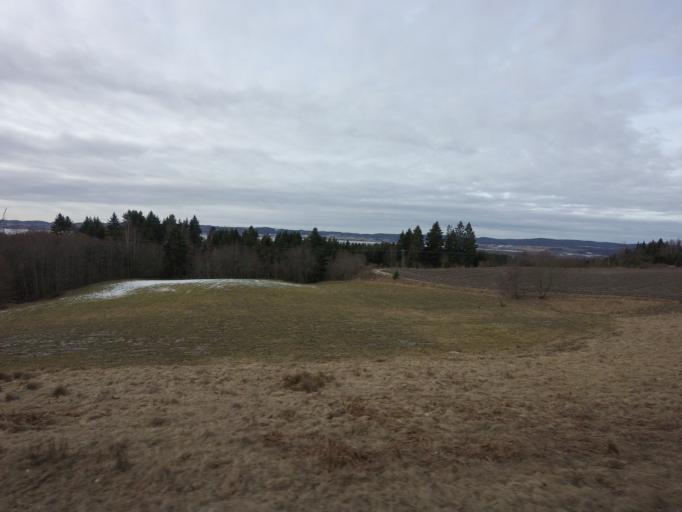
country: NO
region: Akershus
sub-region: Fet
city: Fetsund
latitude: 59.8863
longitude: 11.2051
